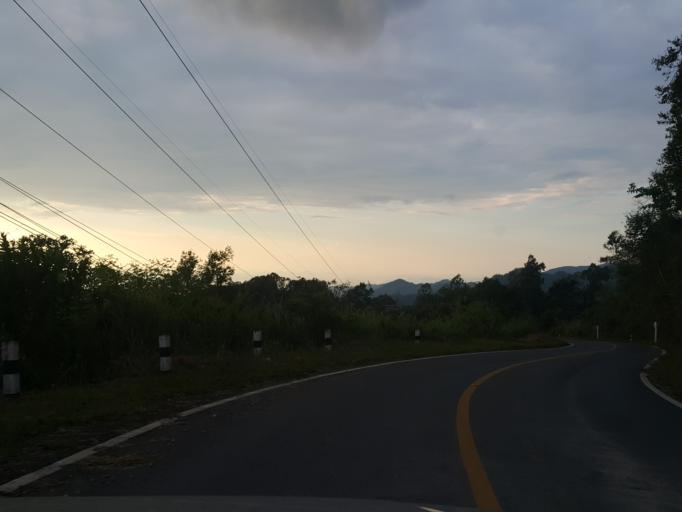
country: TH
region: Mae Hong Son
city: Khun Yuam
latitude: 18.7965
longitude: 98.0835
